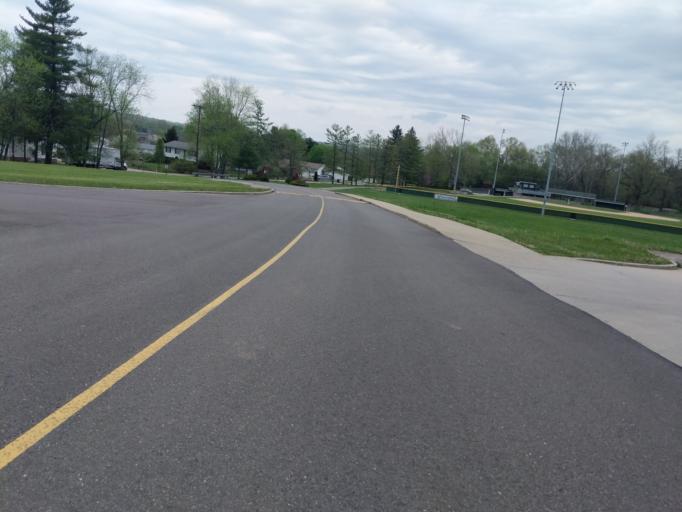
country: US
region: Ohio
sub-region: Athens County
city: The Plains
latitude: 39.3734
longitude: -82.1293
